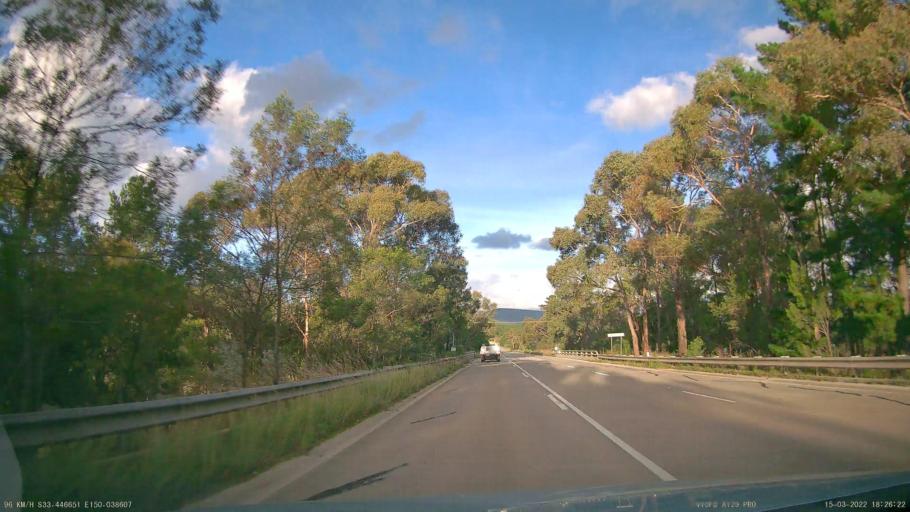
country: AU
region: New South Wales
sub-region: Lithgow
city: Lithgow
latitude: -33.4466
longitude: 150.0392
